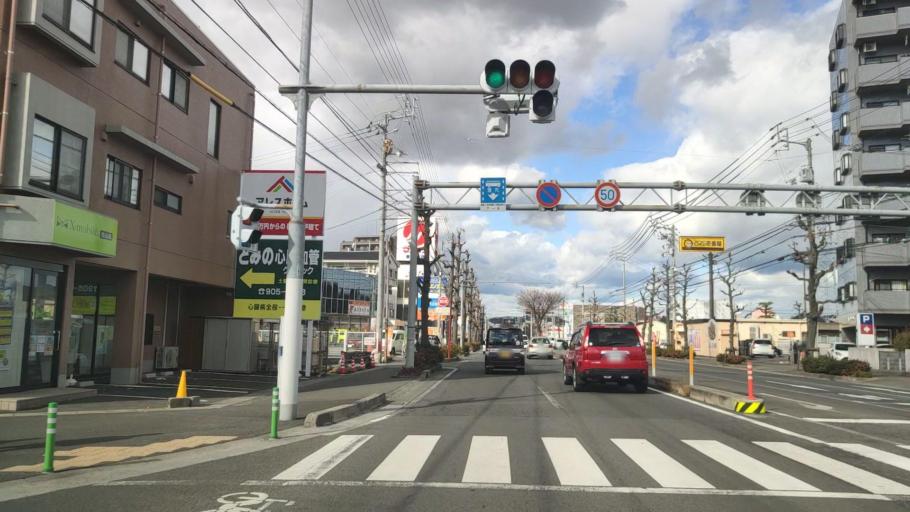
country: JP
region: Ehime
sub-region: Shikoku-chuo Shi
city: Matsuyama
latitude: 33.8120
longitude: 132.7788
